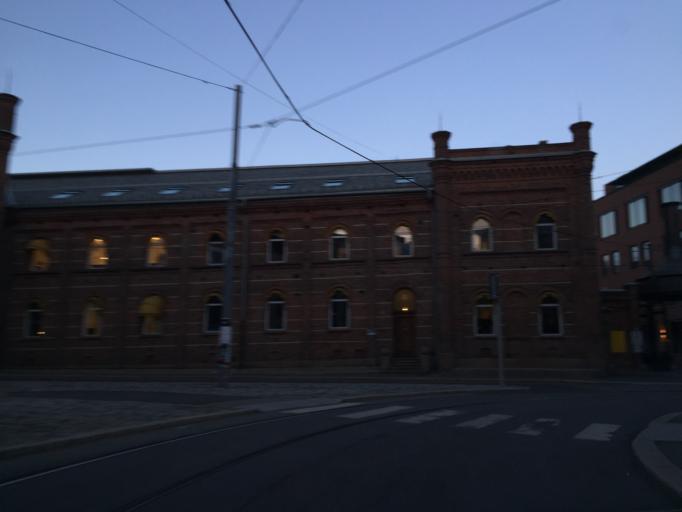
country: NO
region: Oslo
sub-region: Oslo
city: Oslo
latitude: 59.9222
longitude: 10.7315
